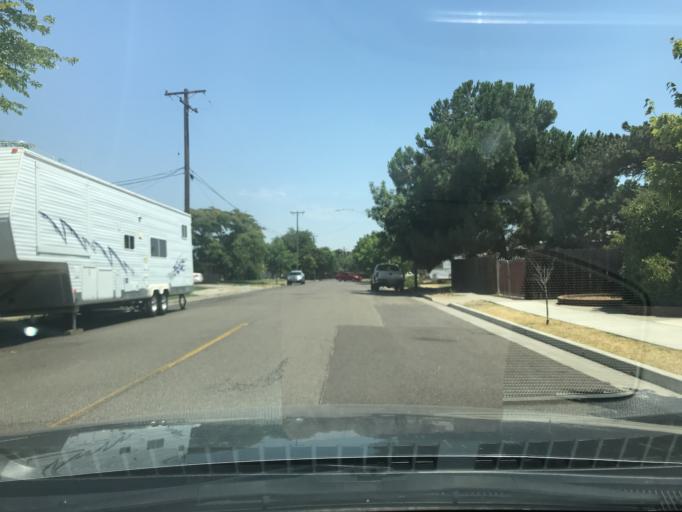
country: US
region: California
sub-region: Merced County
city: Atwater
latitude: 37.3560
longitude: -120.6060
